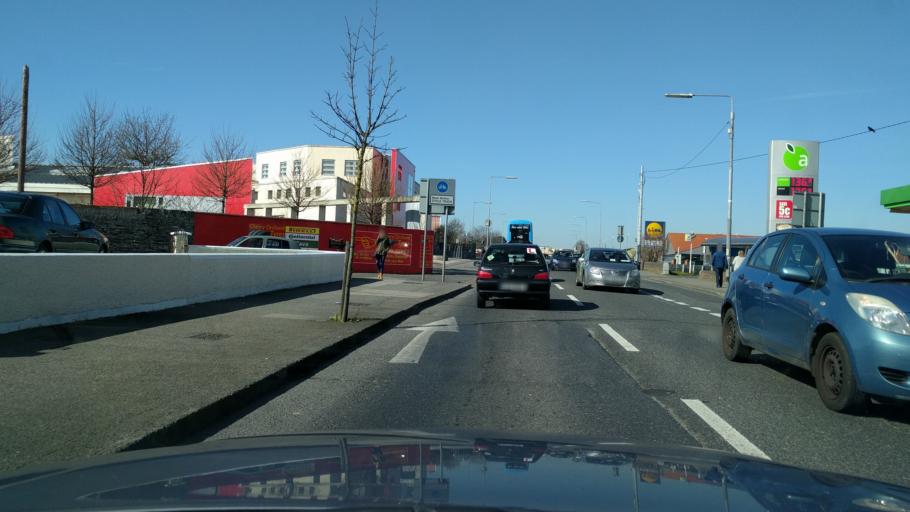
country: IE
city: Palmerstown
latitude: 53.3436
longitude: -6.3700
